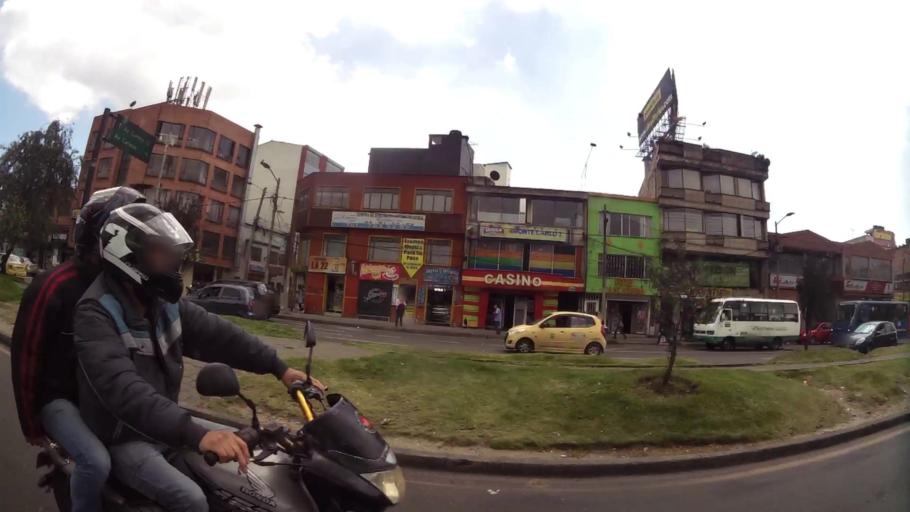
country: CO
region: Bogota D.C.
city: Bogota
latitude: 4.5821
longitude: -74.1032
